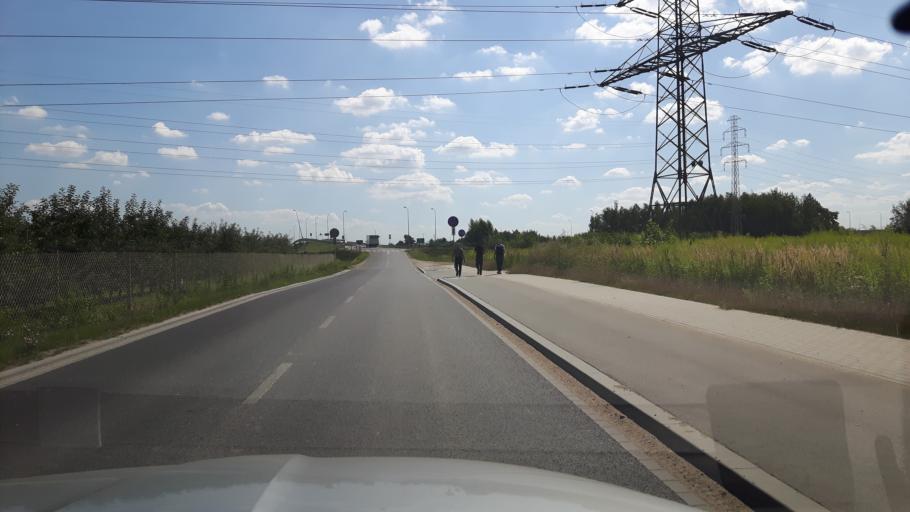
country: PL
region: Masovian Voivodeship
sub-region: Powiat pruszkowski
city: Michalowice
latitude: 52.1301
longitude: 20.8724
